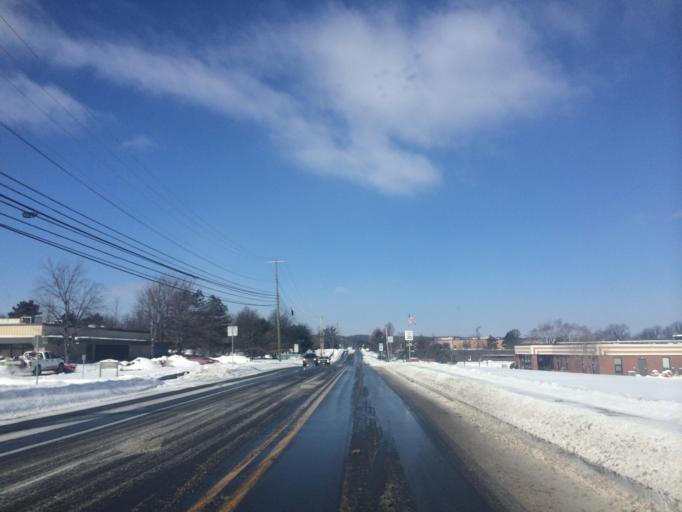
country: US
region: Pennsylvania
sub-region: Centre County
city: Park Forest Village
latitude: 40.7788
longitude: -77.8964
